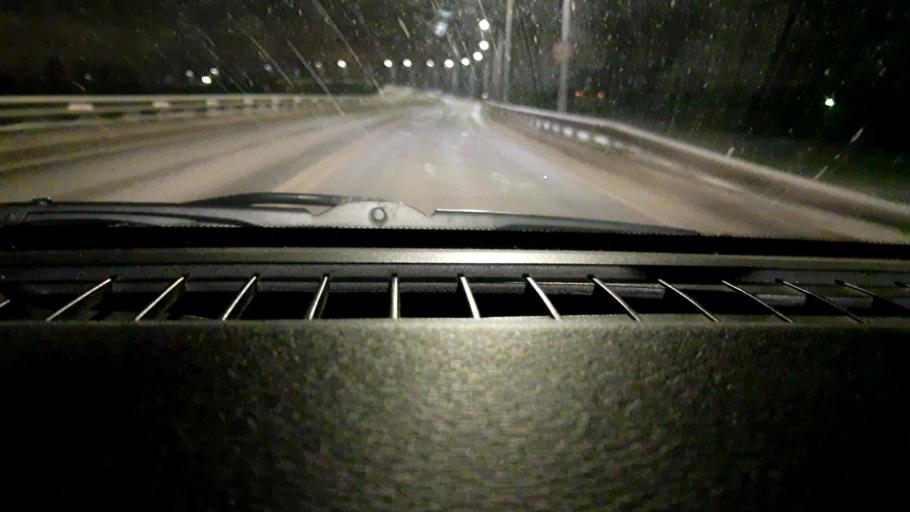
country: RU
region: Nizjnij Novgorod
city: Neklyudovo
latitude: 56.4209
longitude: 43.9889
